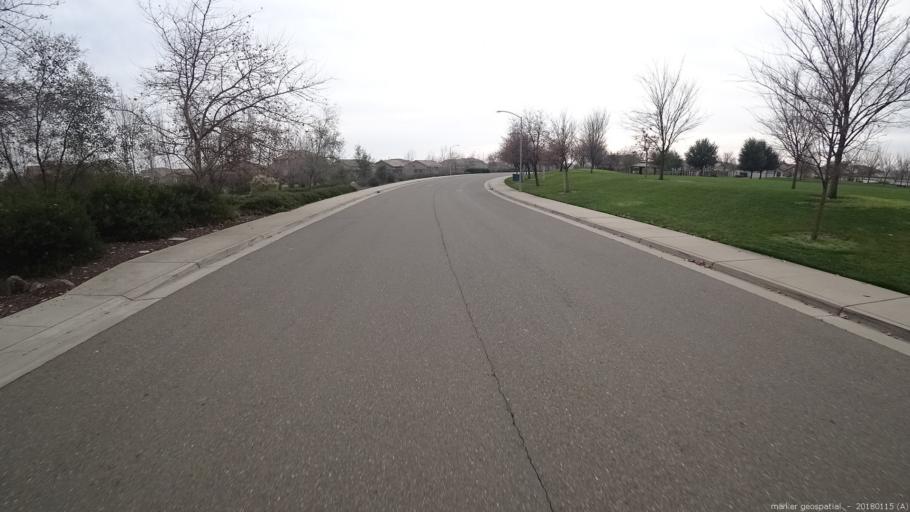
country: US
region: California
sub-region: Sacramento County
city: Rancho Cordova
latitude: 38.5788
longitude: -121.2707
